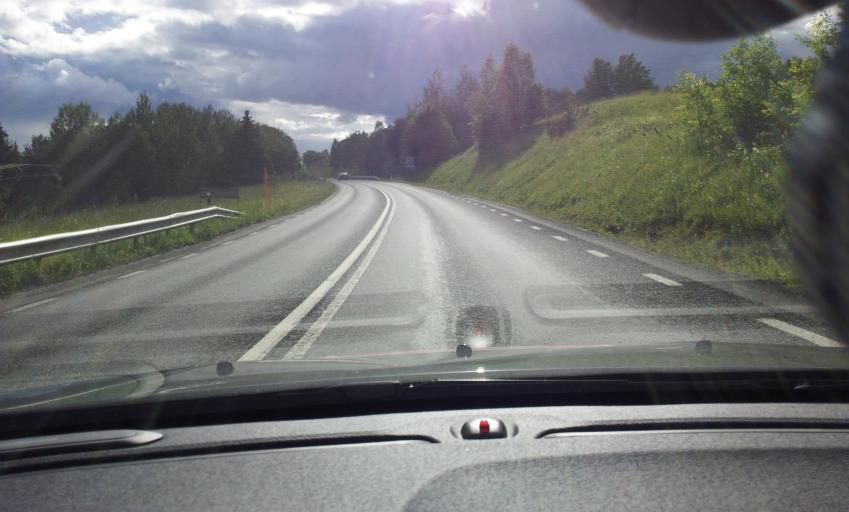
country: SE
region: Jaemtland
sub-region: Are Kommun
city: Jarpen
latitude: 63.3204
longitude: 13.3580
